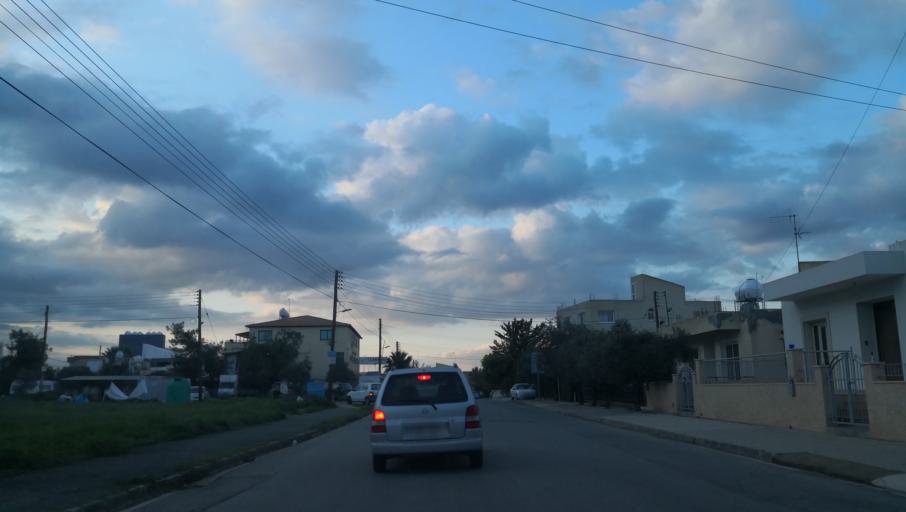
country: CY
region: Lefkosia
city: Kato Deftera
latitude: 35.0990
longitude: 33.3007
